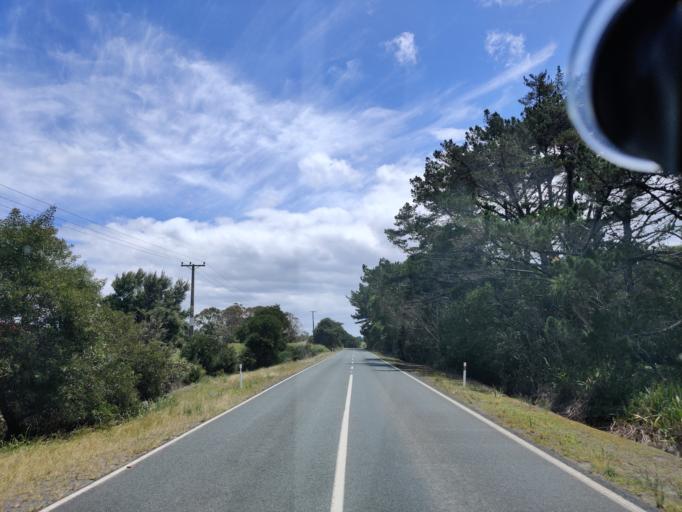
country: NZ
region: Northland
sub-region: Far North District
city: Kaitaia
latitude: -34.7412
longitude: 173.0464
